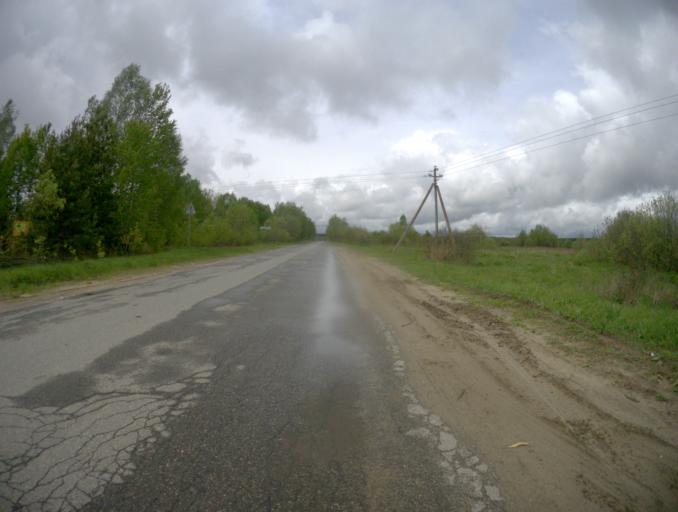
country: RU
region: Vladimir
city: Zolotkovo
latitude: 55.3370
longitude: 41.0152
